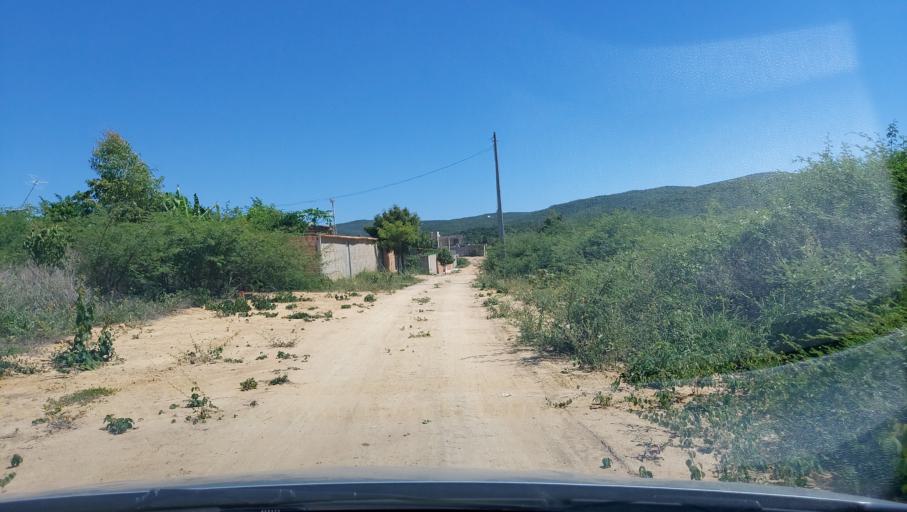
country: BR
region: Bahia
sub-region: Oliveira Dos Brejinhos
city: Beira Rio
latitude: -12.0082
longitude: -42.6288
